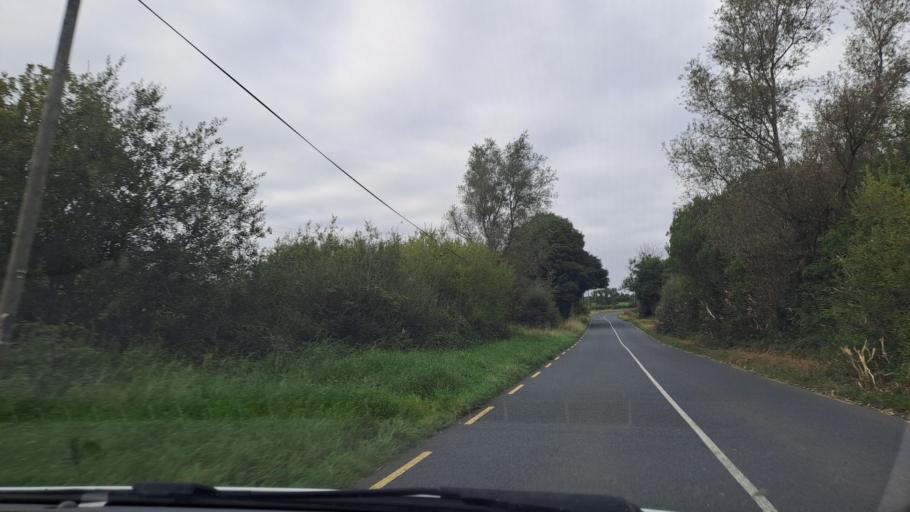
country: IE
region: Ulster
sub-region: County Monaghan
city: Carrickmacross
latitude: 54.0240
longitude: -6.7782
